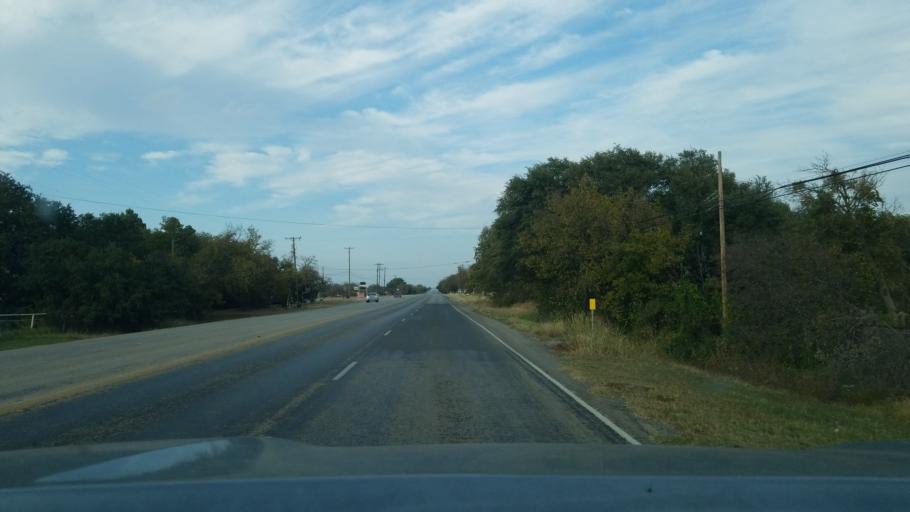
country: US
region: Texas
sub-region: Brown County
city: Early
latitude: 31.7550
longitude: -98.9604
